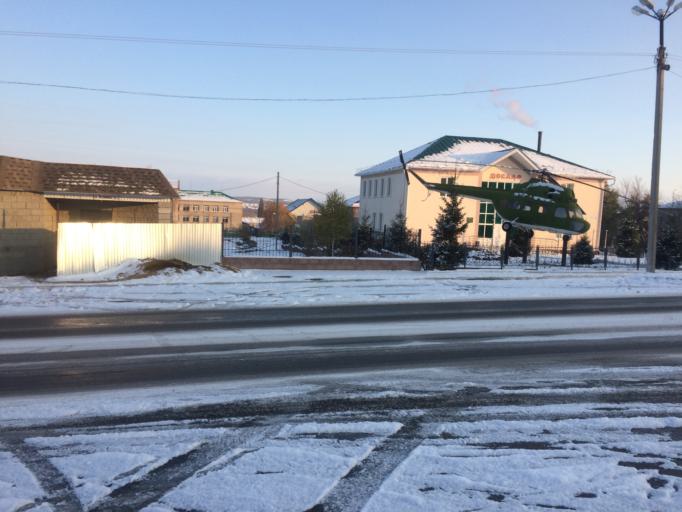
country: RU
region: Bashkortostan
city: Abzakovo
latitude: 53.3394
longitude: 58.5068
